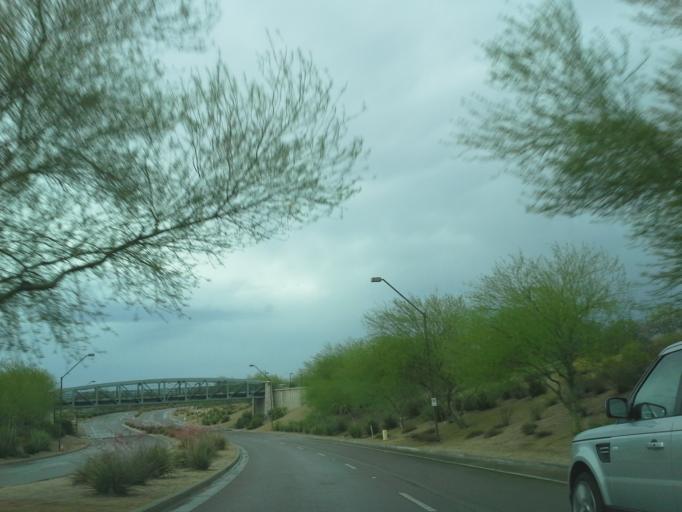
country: US
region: Arizona
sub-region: Maricopa County
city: Paradise Valley
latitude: 33.6443
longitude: -111.9036
